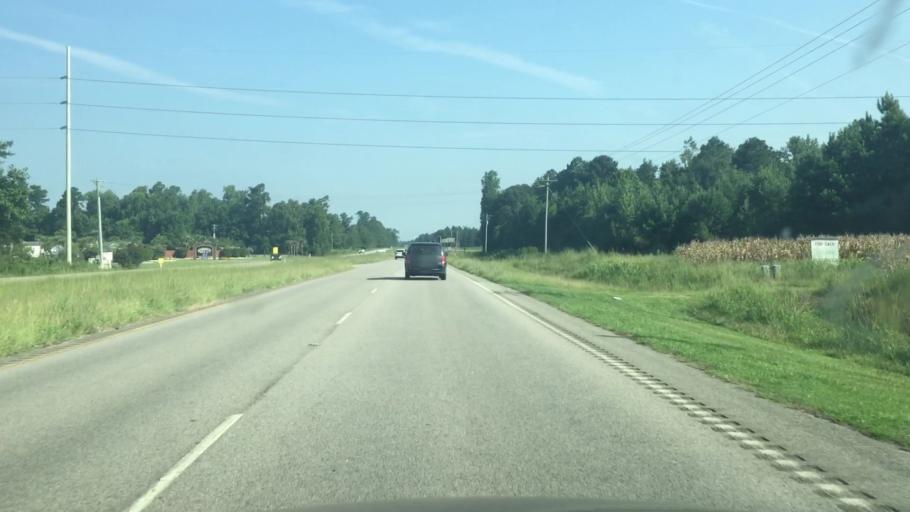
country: US
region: South Carolina
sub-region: Horry County
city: Little River
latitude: 33.9645
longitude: -78.7388
